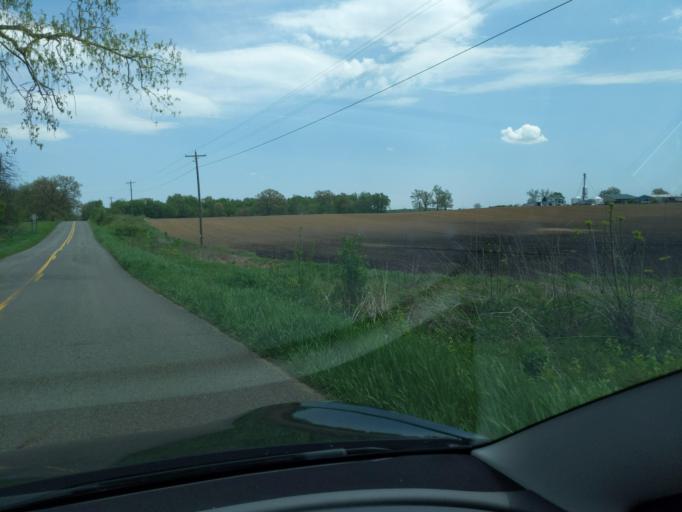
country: US
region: Michigan
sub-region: Ingham County
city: Stockbridge
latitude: 42.4540
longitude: -84.2147
